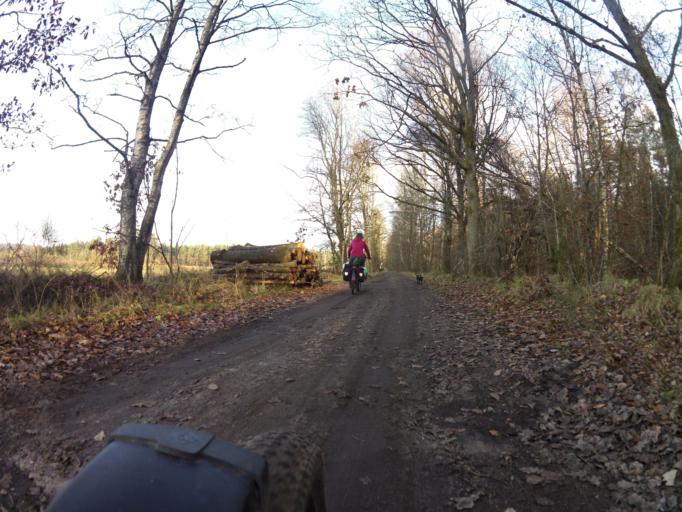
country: PL
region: West Pomeranian Voivodeship
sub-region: Powiat koszalinski
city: Polanow
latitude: 54.1099
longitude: 16.6522
